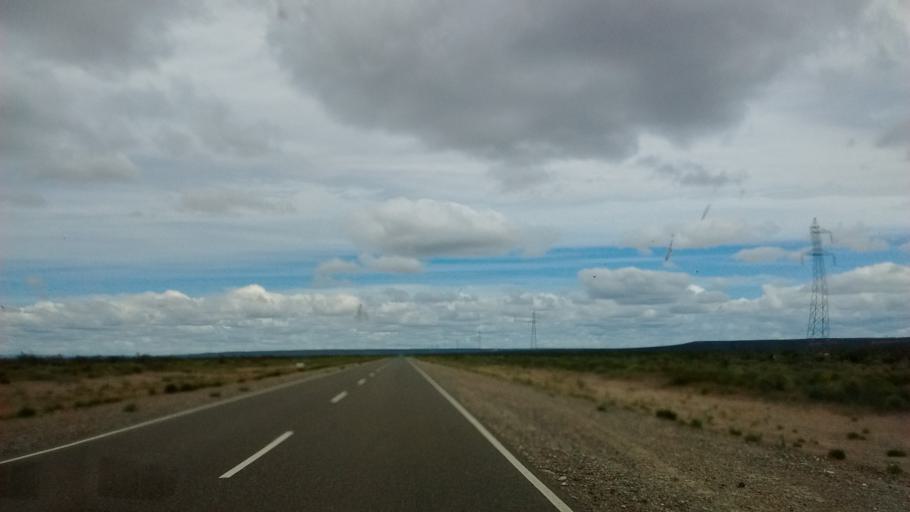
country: AR
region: Neuquen
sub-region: Departamento de Picun Leufu
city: Picun Leufu
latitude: -39.6660
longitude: -69.4354
